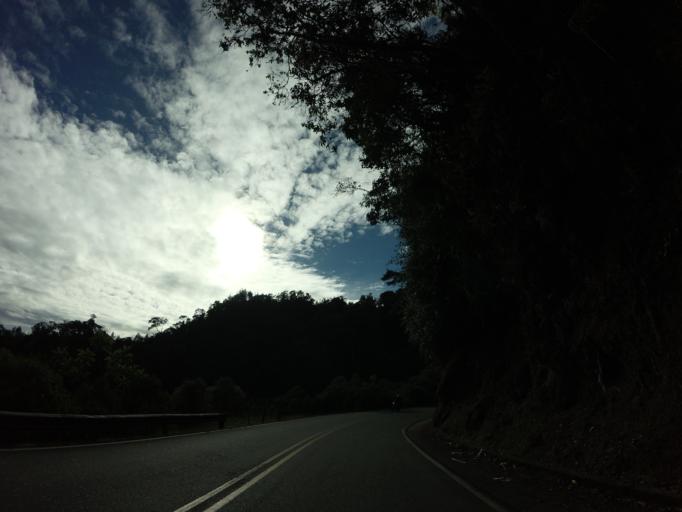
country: CO
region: Tolima
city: Herveo
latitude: 5.1427
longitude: -75.1552
